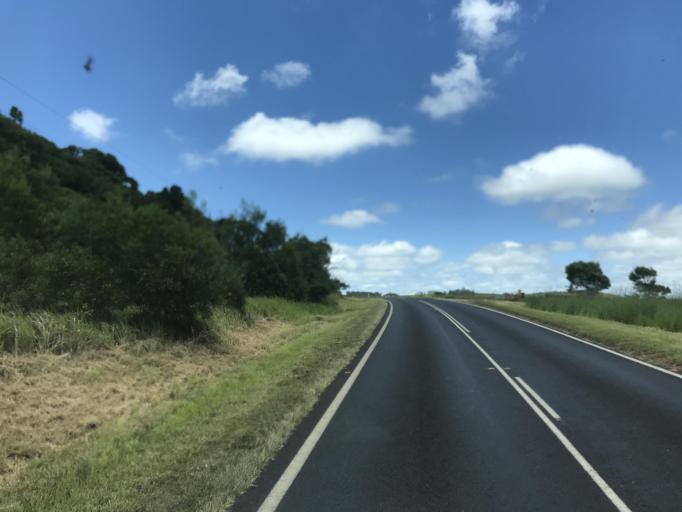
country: AU
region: Queensland
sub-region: Tablelands
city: Ravenshoe
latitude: -17.4979
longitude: 145.4769
